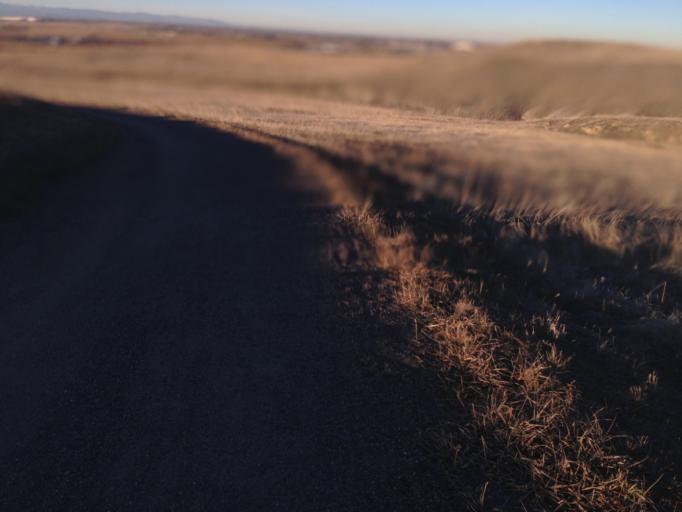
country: US
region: Colorado
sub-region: Broomfield County
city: Broomfield
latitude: 39.9440
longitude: -105.0869
